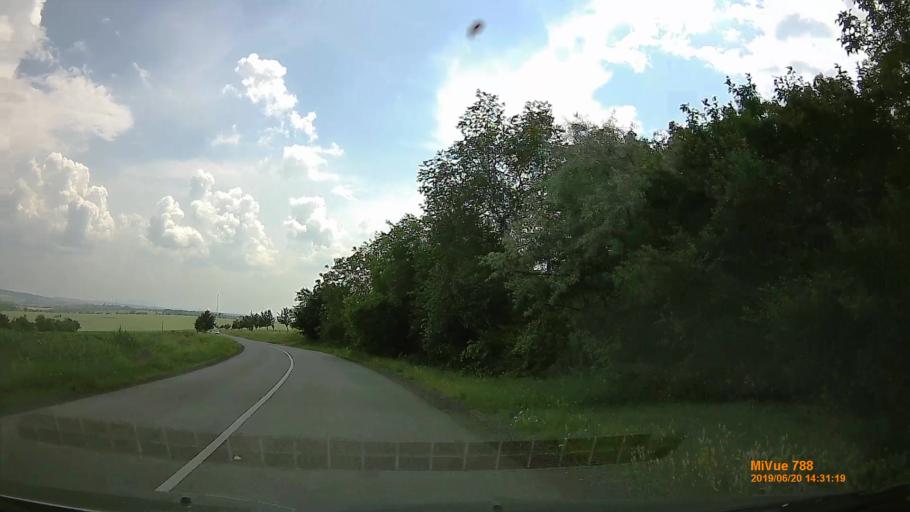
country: HU
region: Baranya
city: Hosszuheteny
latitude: 46.1403
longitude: 18.3478
